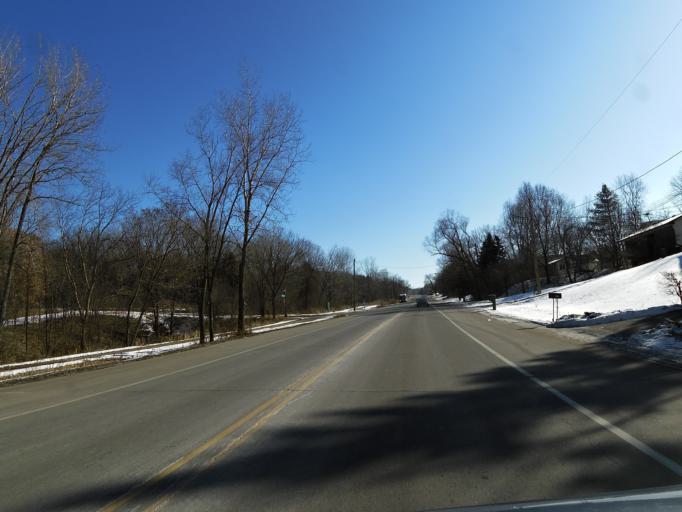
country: US
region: Minnesota
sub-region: Ramsey County
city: Maplewood
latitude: 44.9330
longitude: -93.0109
